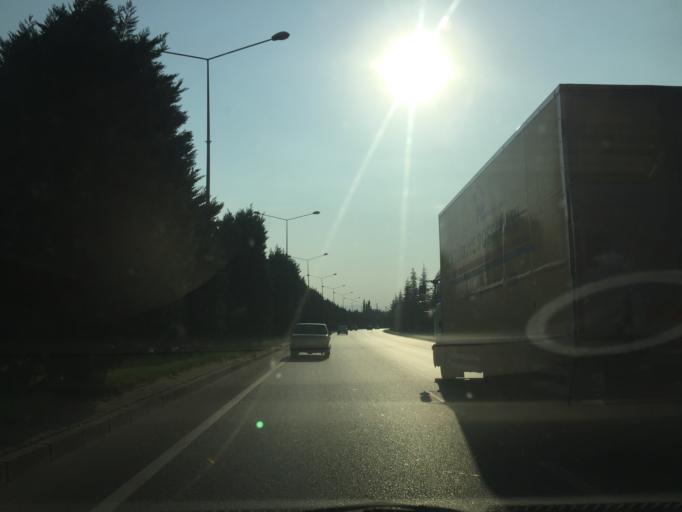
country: TR
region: Manisa
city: Salihli
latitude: 38.4898
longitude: 28.1583
